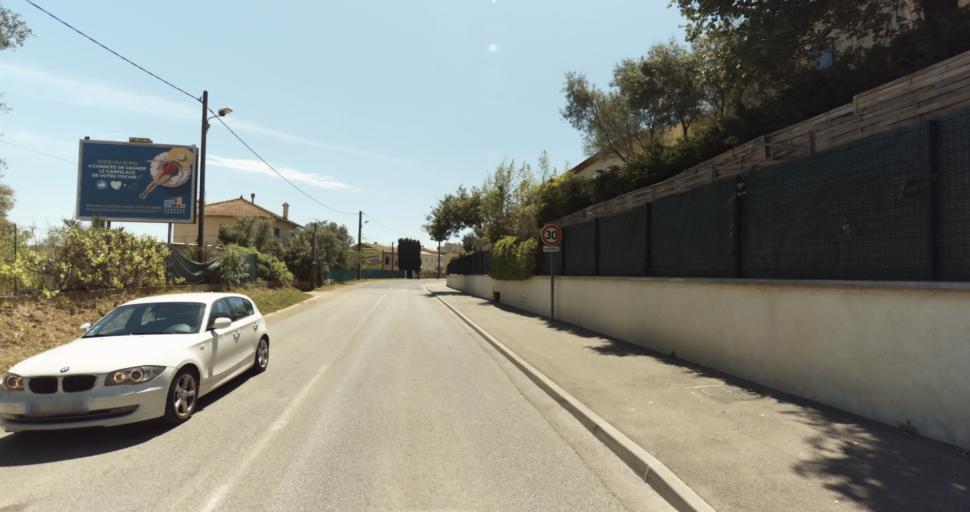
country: FR
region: Provence-Alpes-Cote d'Azur
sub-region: Departement du Var
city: Hyeres
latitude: 43.1277
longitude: 6.1532
